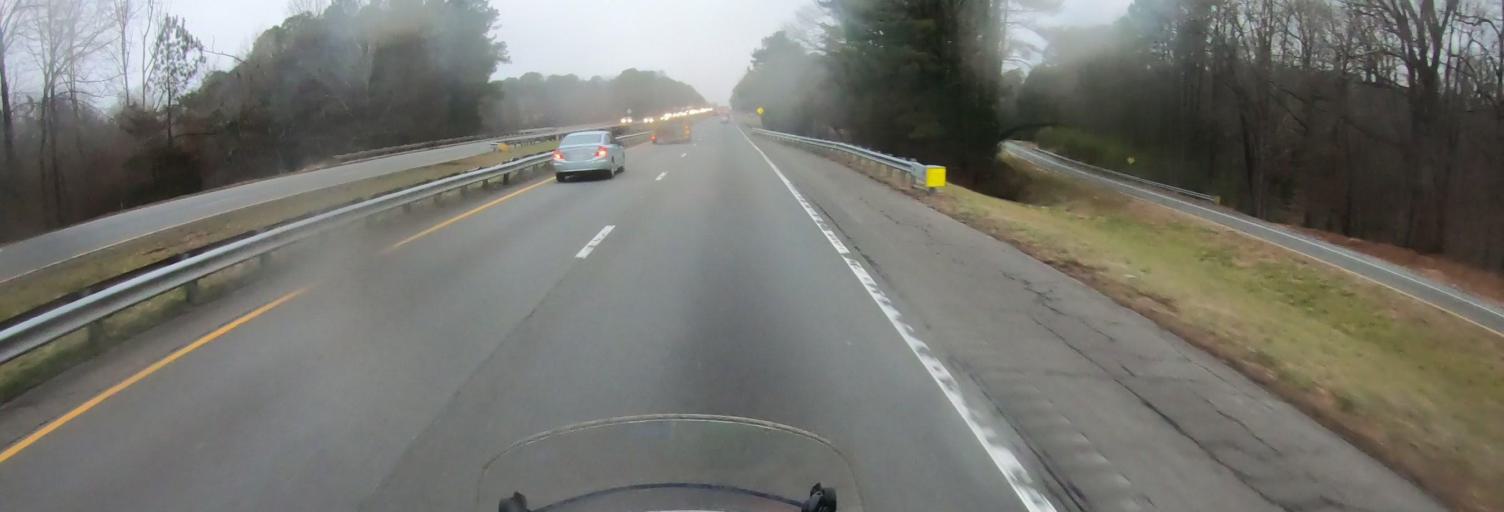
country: US
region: North Carolina
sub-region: Orange County
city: Hillsborough
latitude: 36.0376
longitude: -79.0051
